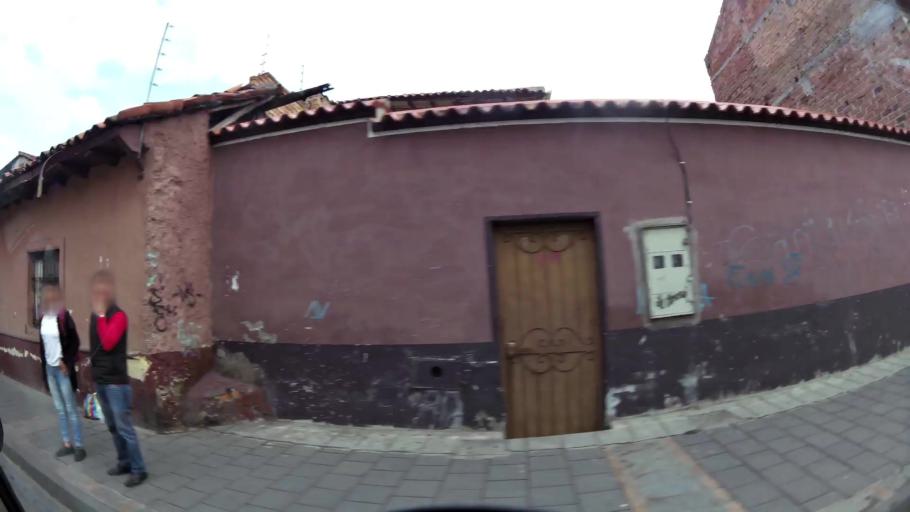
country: EC
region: Azuay
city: Cuenca
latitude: -2.8918
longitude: -79.0041
